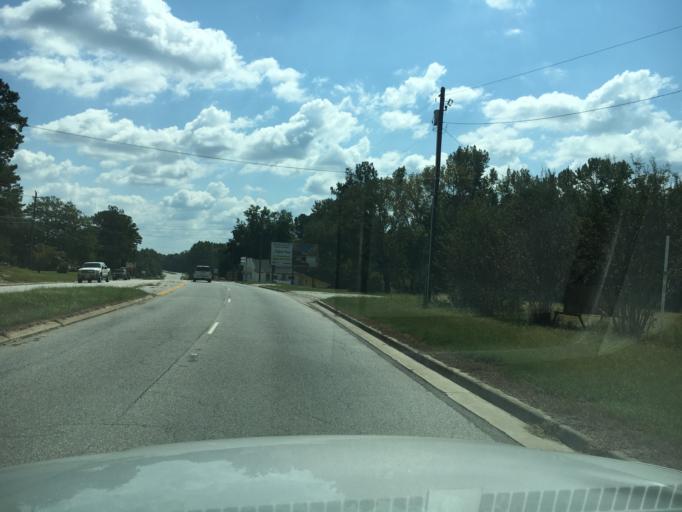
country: US
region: South Carolina
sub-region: Greenwood County
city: Greenwood
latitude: 34.2810
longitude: -82.2364
